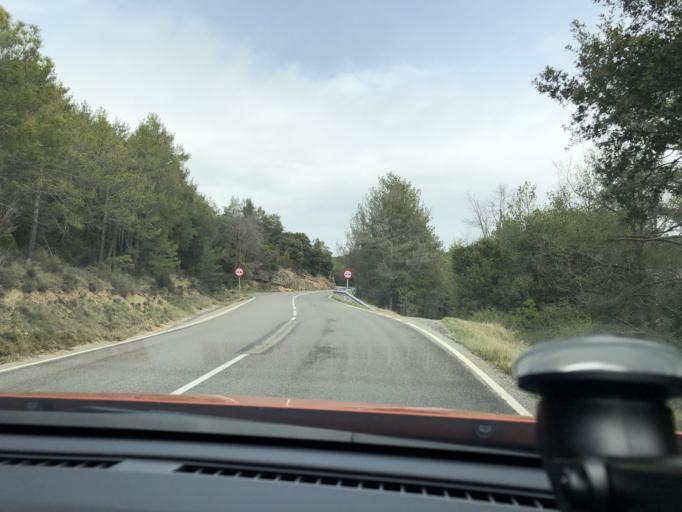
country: ES
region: Catalonia
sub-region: Provincia de Lleida
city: Olius
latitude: 42.0884
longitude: 1.5253
